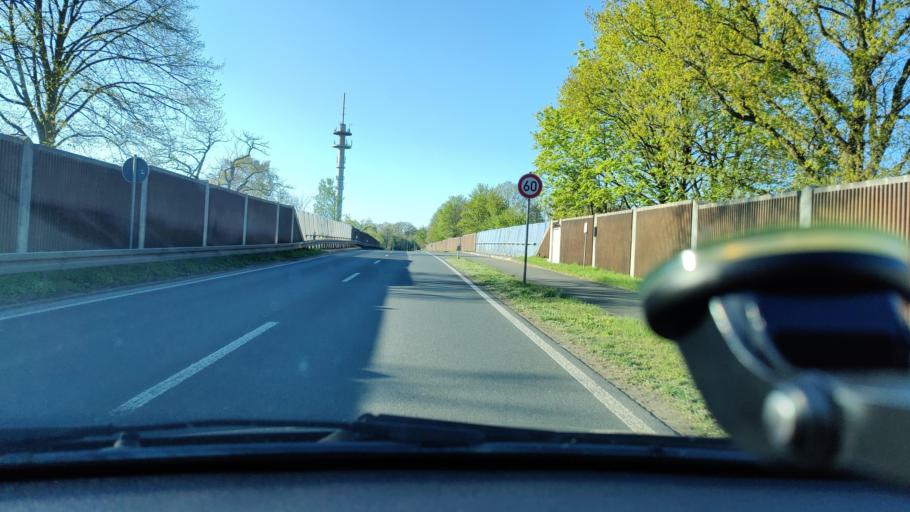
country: DE
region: North Rhine-Westphalia
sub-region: Regierungsbezirk Munster
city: Coesfeld
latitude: 51.9389
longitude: 7.1535
